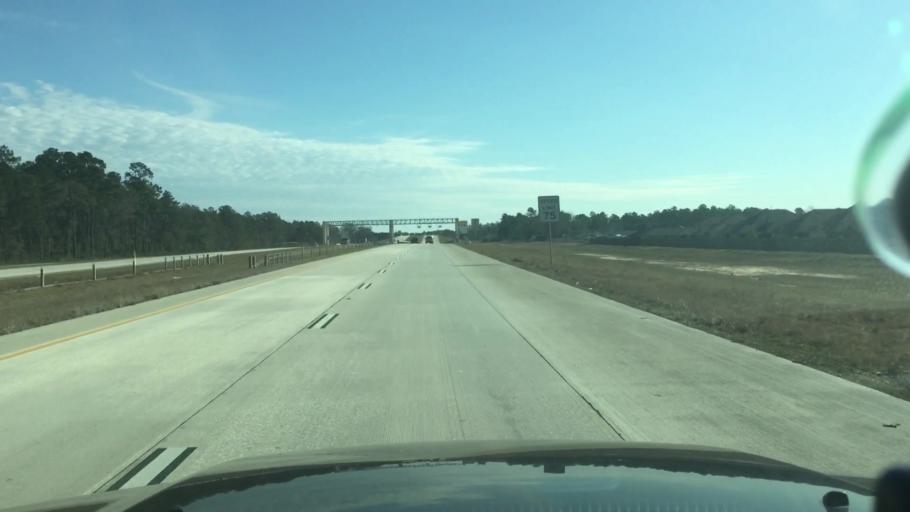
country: US
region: Texas
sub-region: Montgomery County
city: Porter Heights
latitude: 30.1376
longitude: -95.2813
